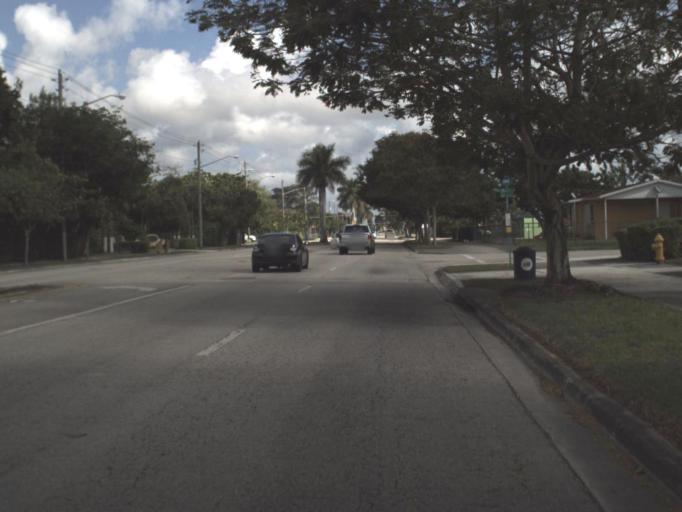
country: US
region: Florida
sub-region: Miami-Dade County
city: Leisure City
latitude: 25.4993
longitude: -80.4424
